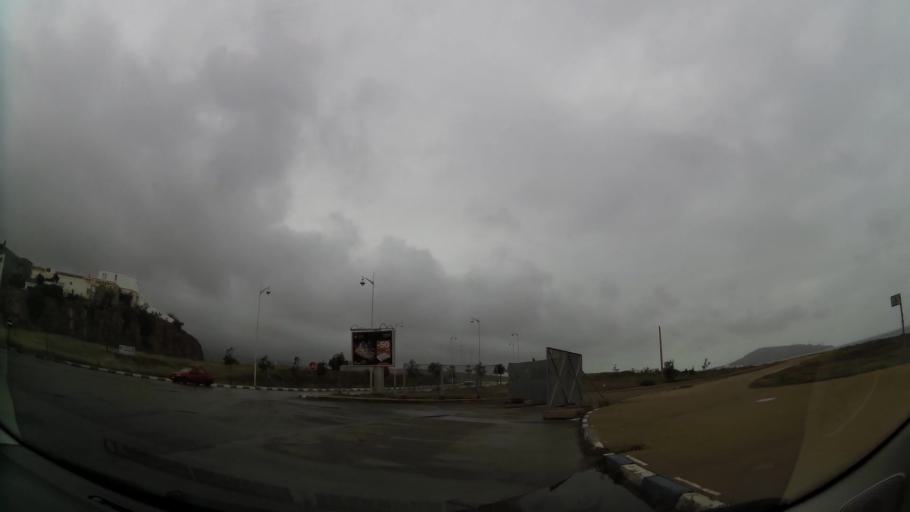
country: MA
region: Oriental
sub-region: Nador
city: Nador
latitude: 35.1881
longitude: -2.9258
